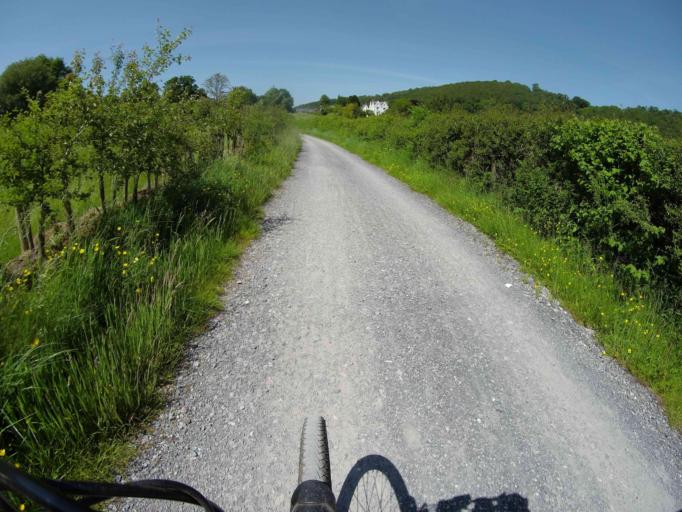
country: GB
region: England
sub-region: Devon
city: Bovey Tracey
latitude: 50.6460
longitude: -3.7403
